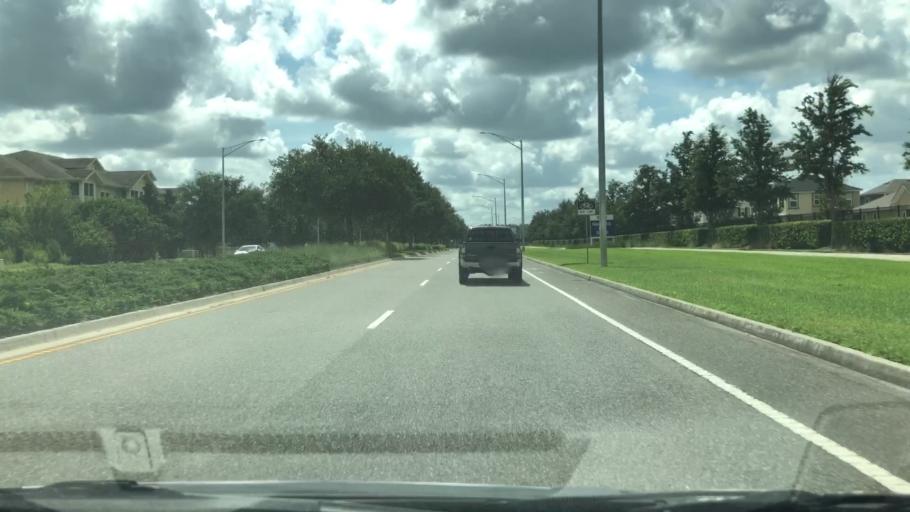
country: US
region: Florida
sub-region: Saint Johns County
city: Fruit Cove
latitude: 30.1156
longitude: -81.5205
